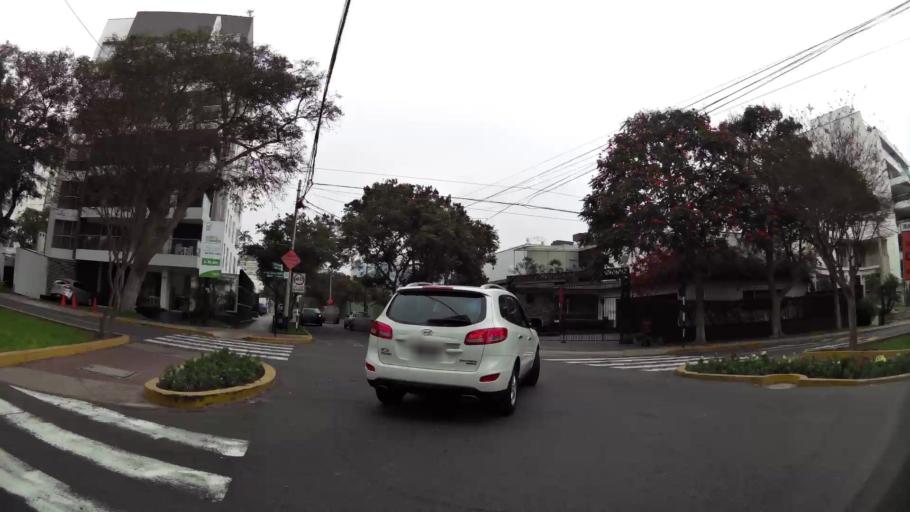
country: PE
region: Lima
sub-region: Lima
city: San Isidro
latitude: -12.0984
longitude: -77.0393
